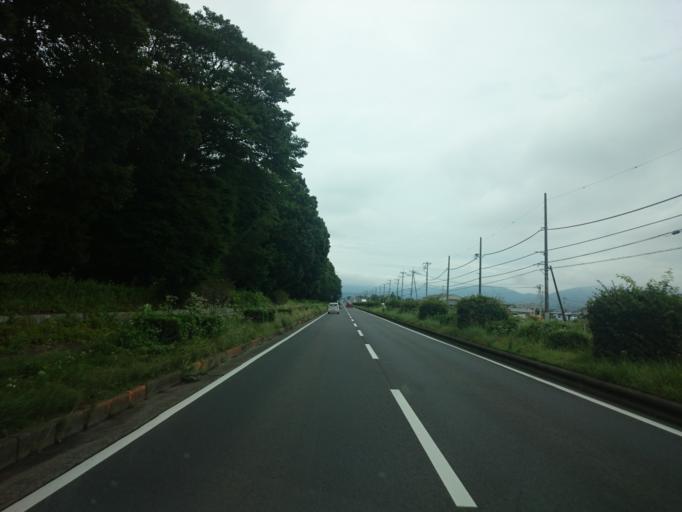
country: JP
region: Ibaraki
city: Tsukuba
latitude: 36.1251
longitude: 140.0748
